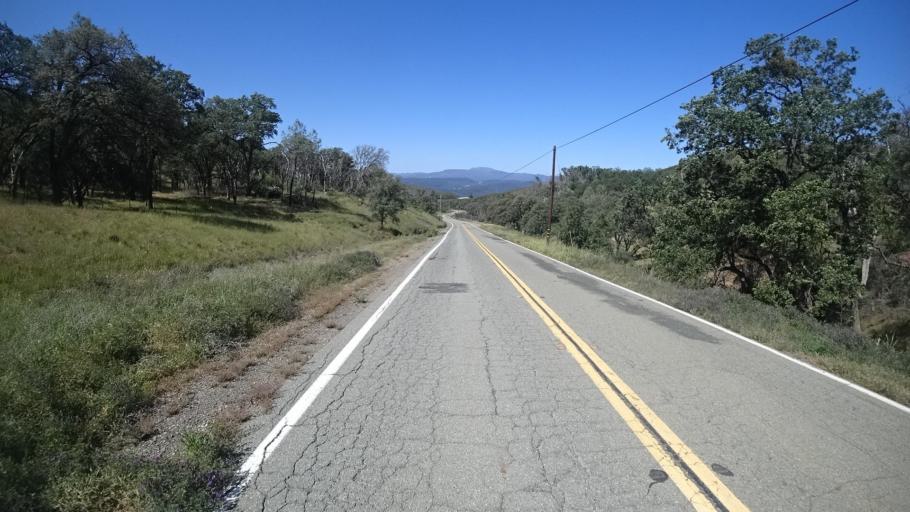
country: US
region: California
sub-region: Lake County
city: Hidden Valley Lake
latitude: 38.8926
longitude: -122.4860
